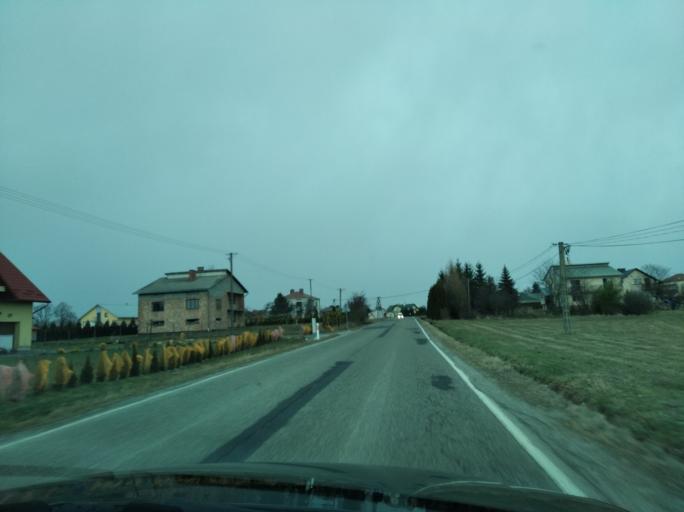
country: PL
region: Subcarpathian Voivodeship
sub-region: Powiat rzeszowski
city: Hyzne
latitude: 49.9212
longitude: 22.1960
